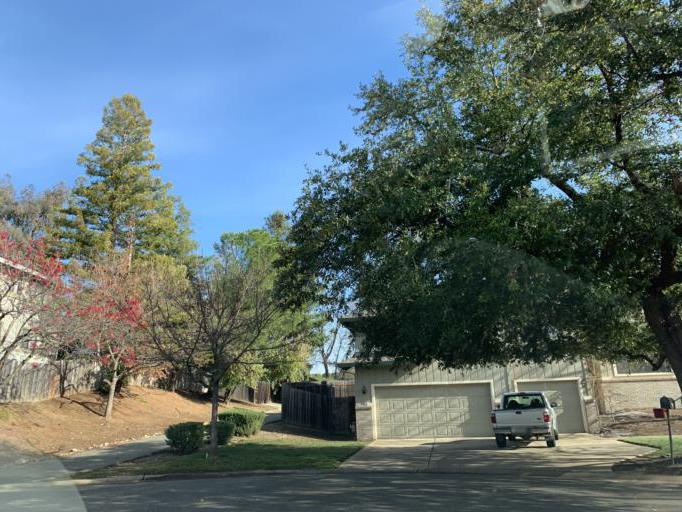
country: US
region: California
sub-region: El Dorado County
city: El Dorado Hills
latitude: 38.6534
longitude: -121.0756
